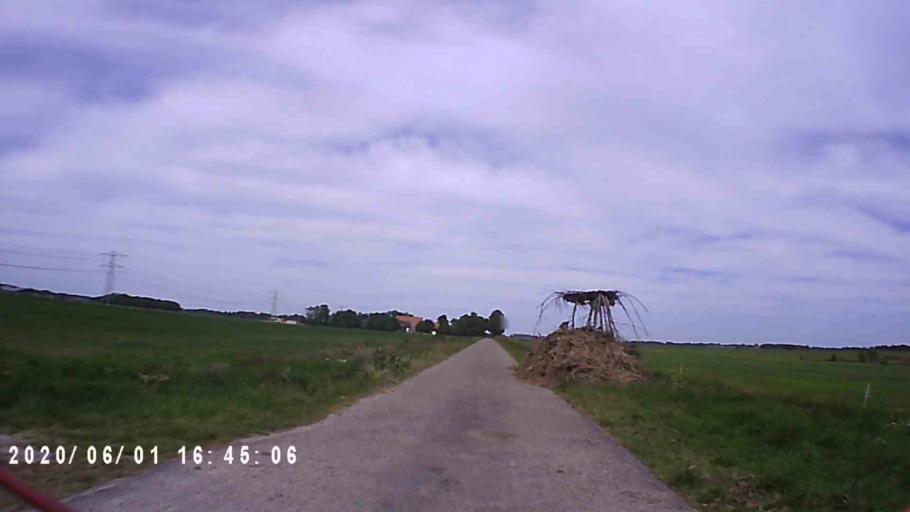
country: NL
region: Friesland
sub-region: Gemeente Tytsjerksteradiel
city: Tytsjerk
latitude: 53.1857
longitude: 5.8861
